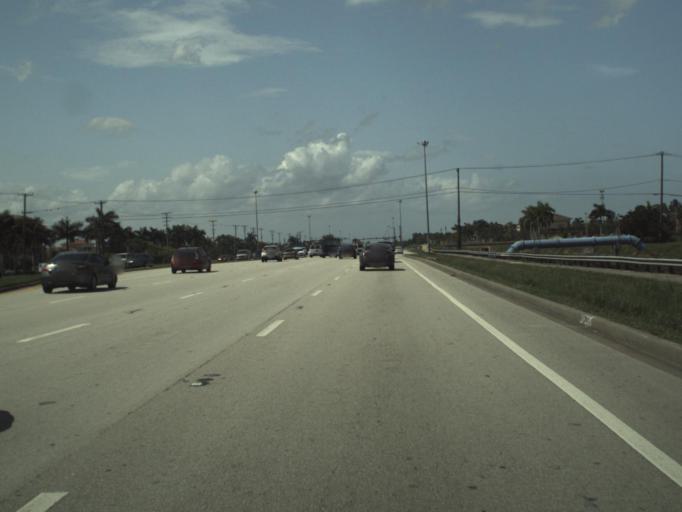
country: US
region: Florida
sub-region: Palm Beach County
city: Wellington
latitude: 26.6603
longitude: -80.2029
